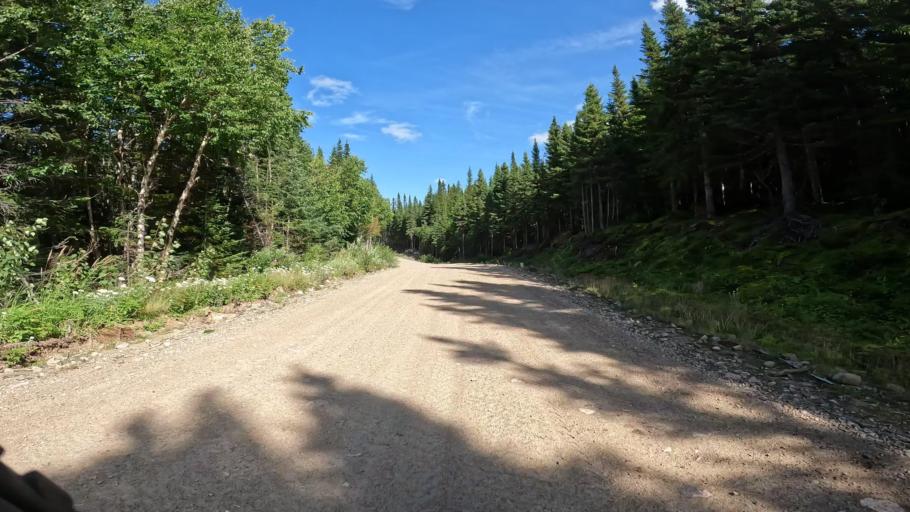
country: CA
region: Quebec
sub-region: Capitale-Nationale
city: Baie-Saint-Paul
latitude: 47.8062
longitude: -70.6739
